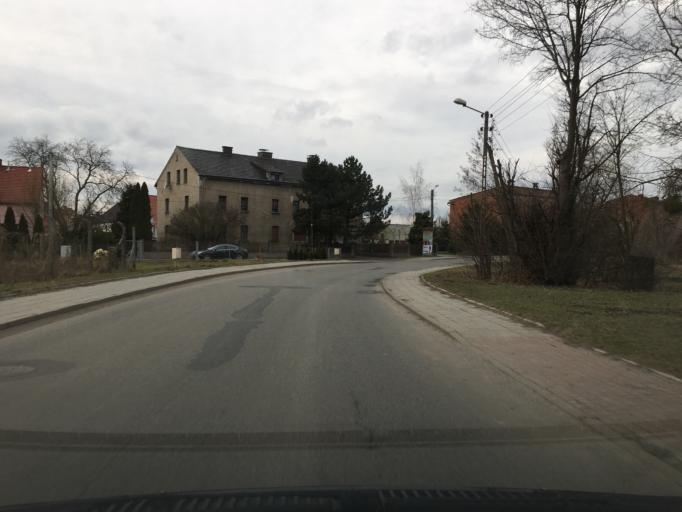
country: PL
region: Opole Voivodeship
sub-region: Powiat kedzierzynsko-kozielski
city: Kozle
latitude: 50.3459
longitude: 18.1437
